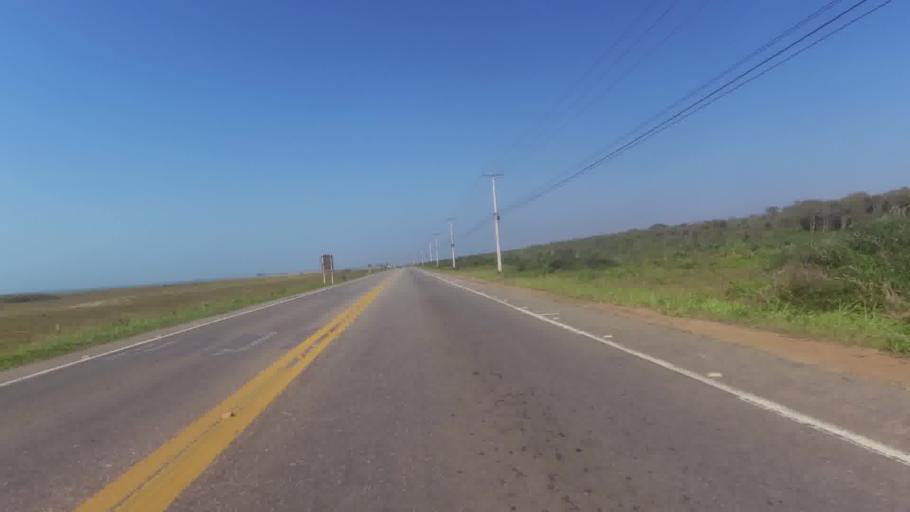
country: BR
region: Espirito Santo
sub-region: Itapemirim
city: Itapemirim
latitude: -20.9678
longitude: -40.8108
